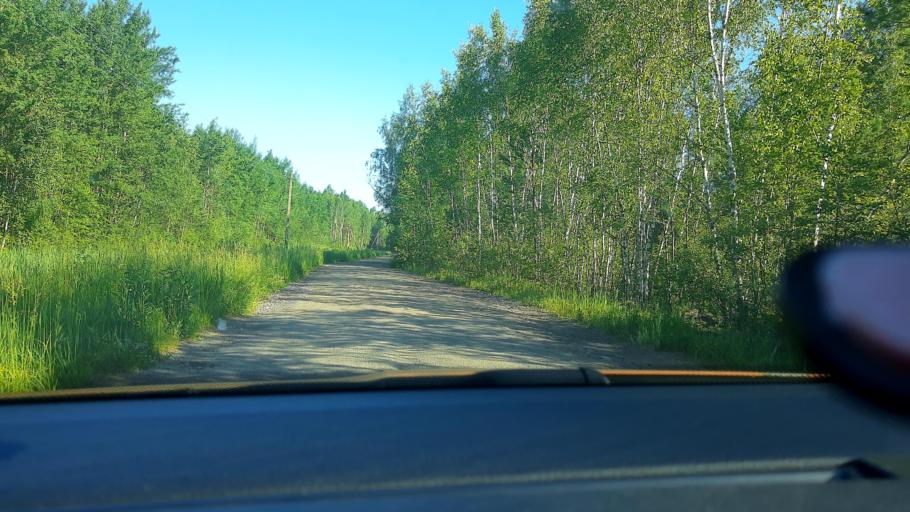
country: RU
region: Moskovskaya
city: Elektrogorsk
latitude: 55.8945
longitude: 38.7174
